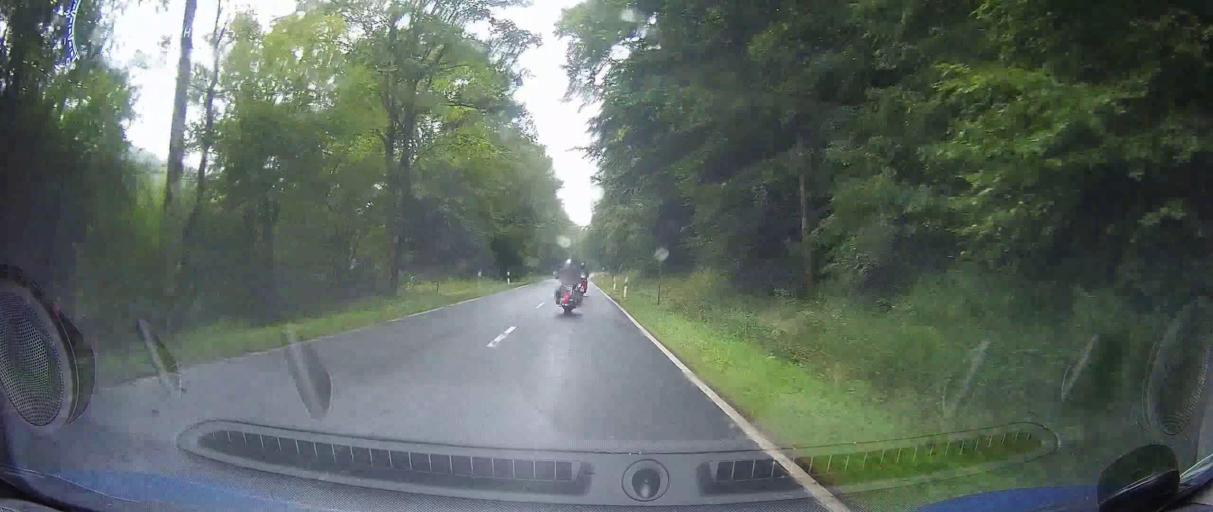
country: DE
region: Lower Saxony
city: Uslar
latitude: 51.7059
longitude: 9.6239
